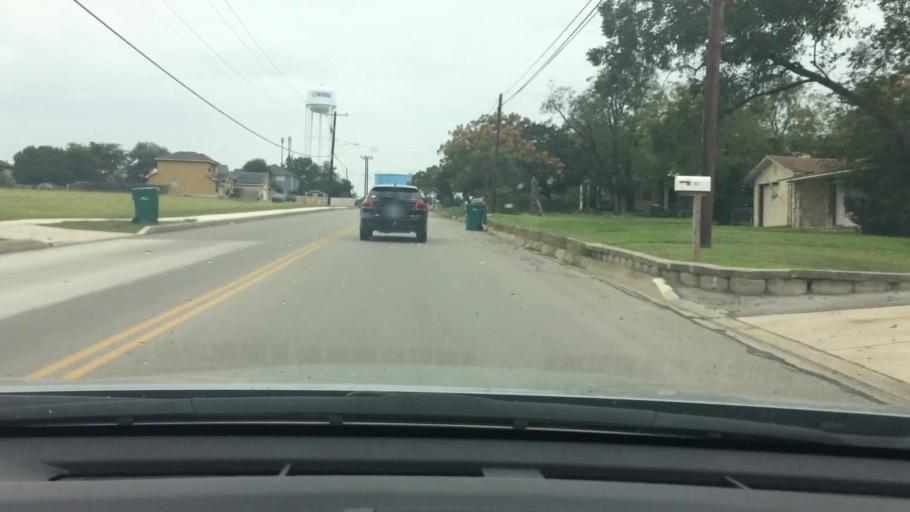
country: US
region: Texas
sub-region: Bexar County
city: Converse
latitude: 29.5239
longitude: -98.3209
